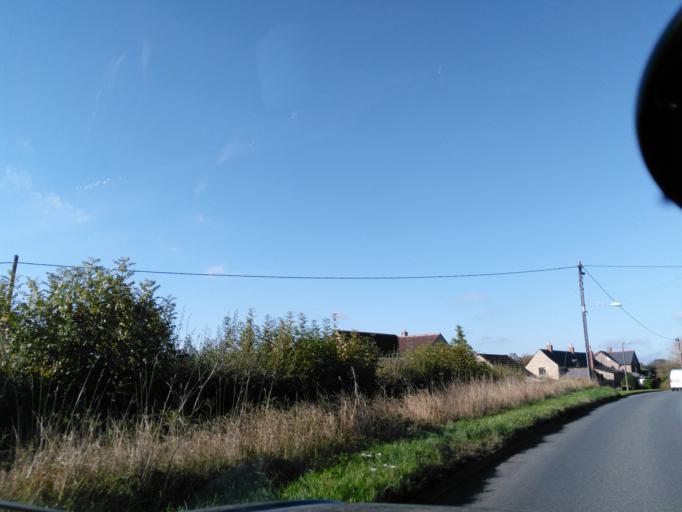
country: GB
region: England
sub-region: Wiltshire
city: Atworth
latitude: 51.3881
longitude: -2.1688
